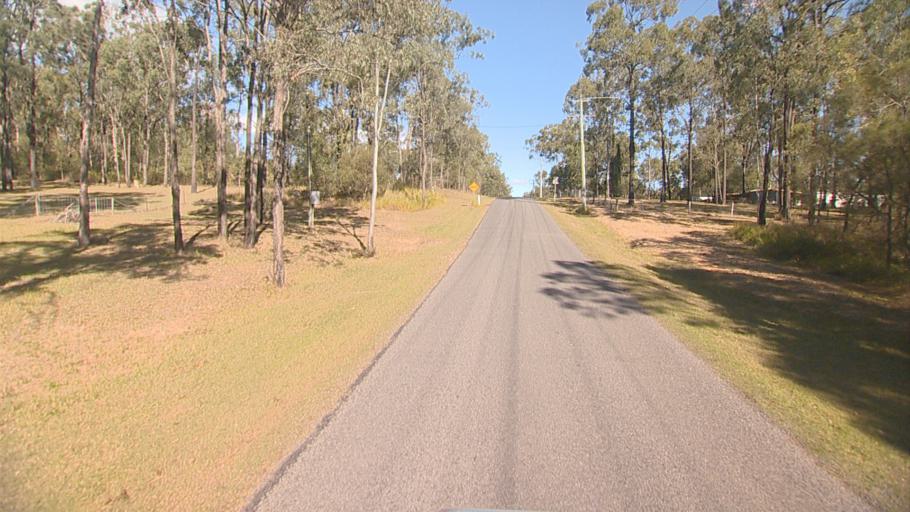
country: AU
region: Queensland
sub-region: Logan
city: Chambers Flat
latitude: -27.8088
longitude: 153.0788
